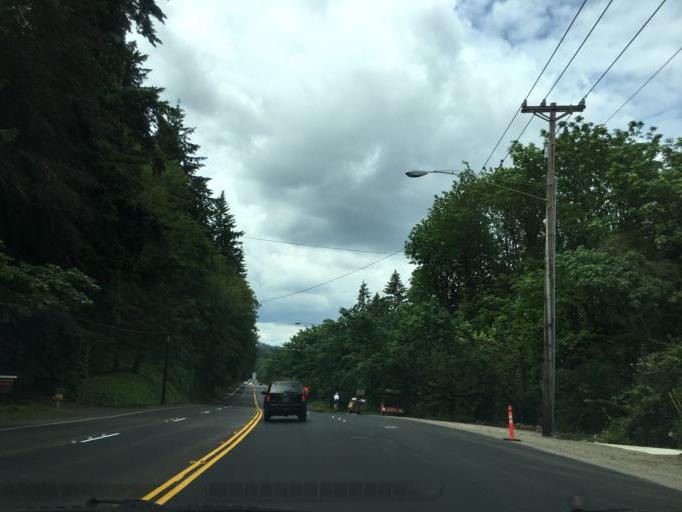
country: US
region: Oregon
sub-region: Clackamas County
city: Milwaukie
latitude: 45.4529
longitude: -122.6602
